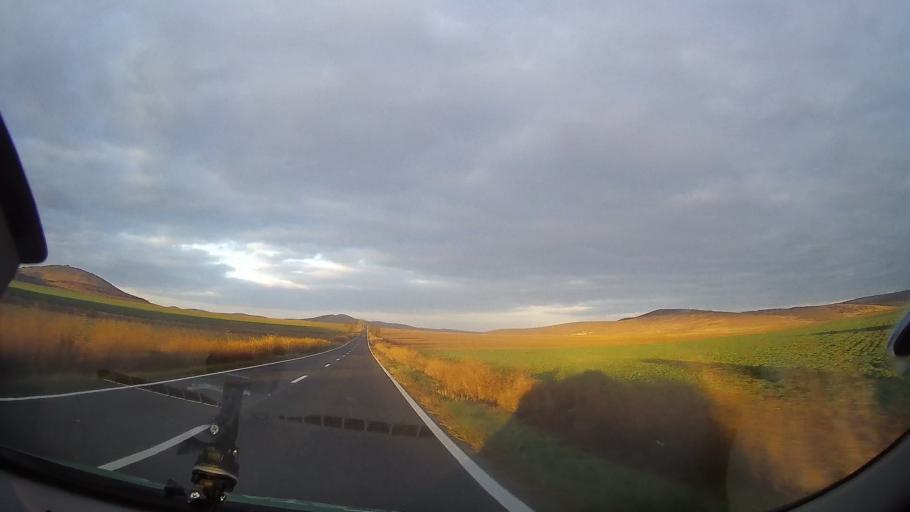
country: RO
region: Tulcea
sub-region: Comuna Nalbant
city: Nicolae Balcescu
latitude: 44.9715
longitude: 28.5402
